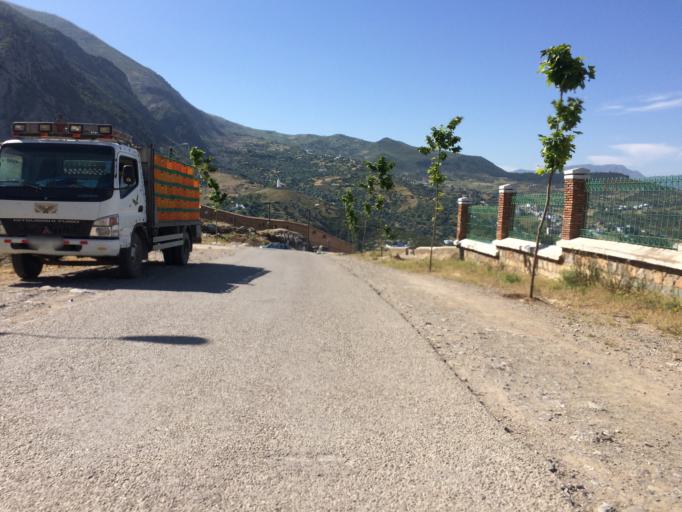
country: MA
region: Tanger-Tetouan
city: Chefchaouene
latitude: 35.1723
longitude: -5.2615
